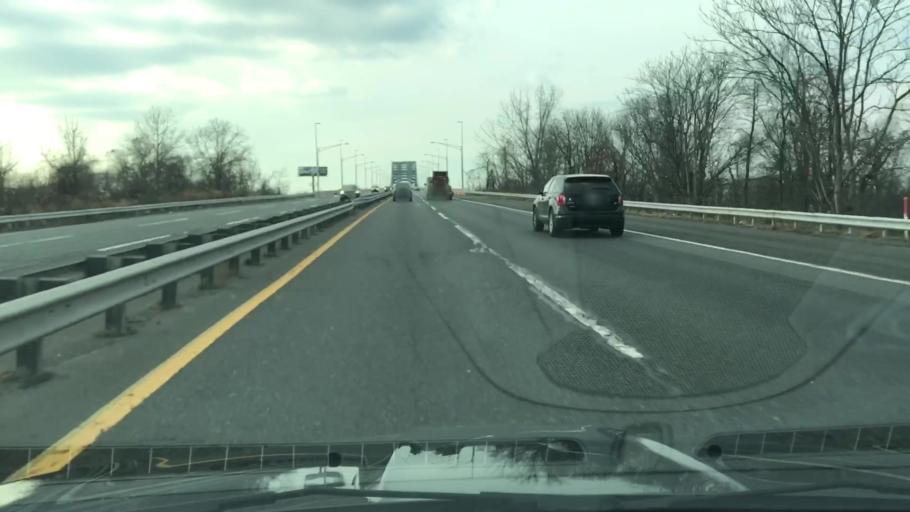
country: US
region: Pennsylvania
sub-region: Bucks County
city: Tullytown
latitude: 40.1139
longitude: -74.8193
